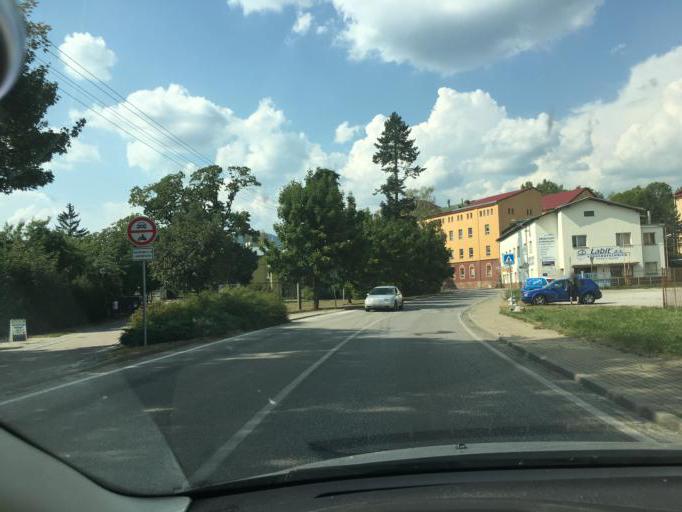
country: CZ
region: Kralovehradecky
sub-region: Okres Trutnov
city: Vrchlabi
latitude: 50.6210
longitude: 15.6172
